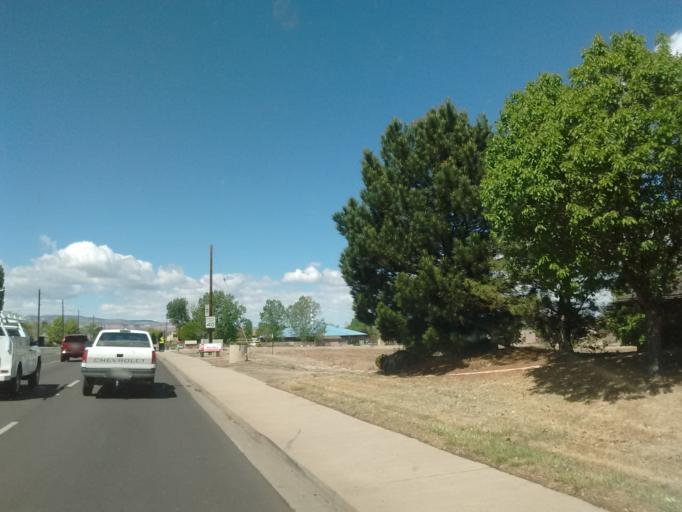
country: US
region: Colorado
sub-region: Mesa County
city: Grand Junction
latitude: 39.0919
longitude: -108.5301
